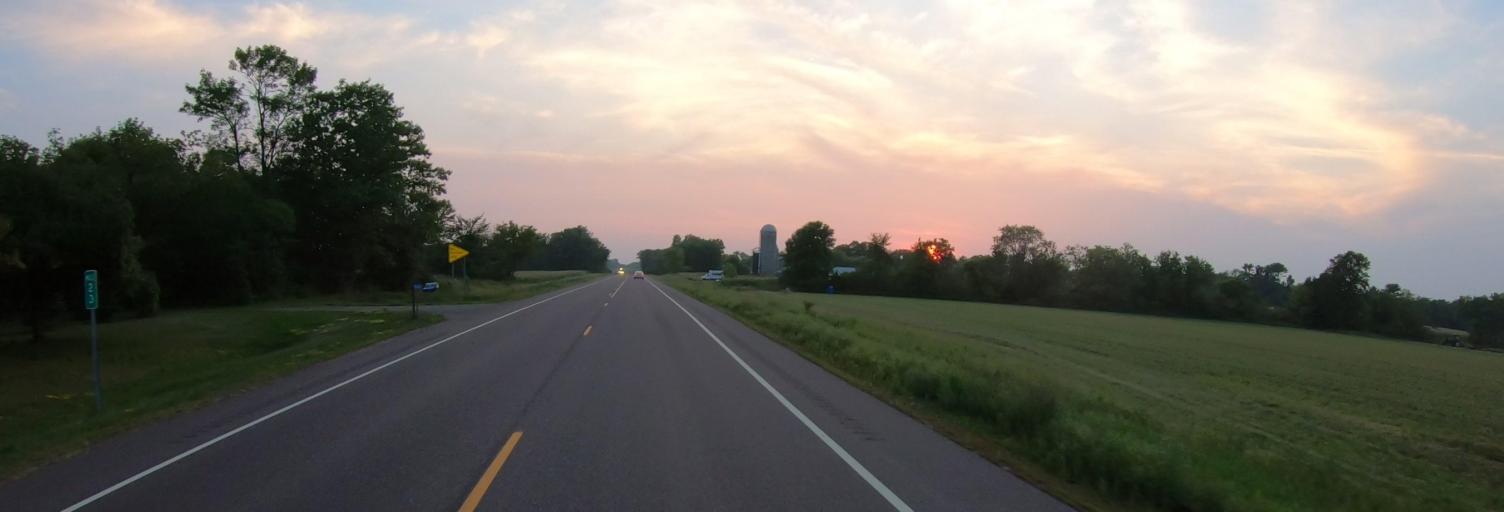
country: US
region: Minnesota
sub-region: Pine County
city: Rock Creek
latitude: 45.7735
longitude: -92.9123
